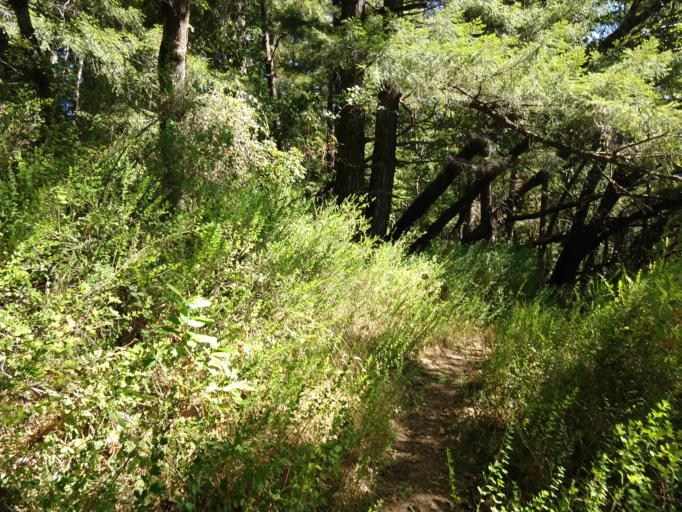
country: US
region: California
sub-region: Humboldt County
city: Rio Dell
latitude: 40.3583
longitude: -123.9975
